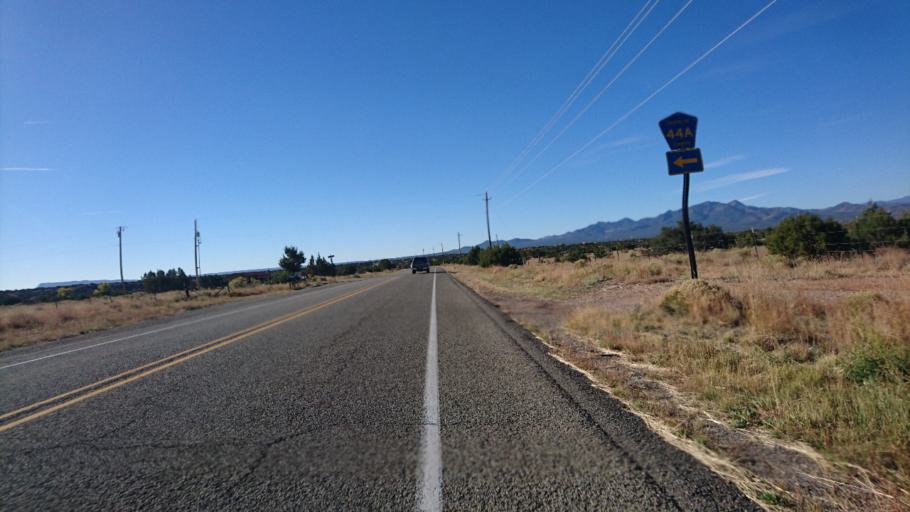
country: US
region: New Mexico
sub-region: Santa Fe County
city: La Cienega
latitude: 35.4657
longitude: -106.0700
